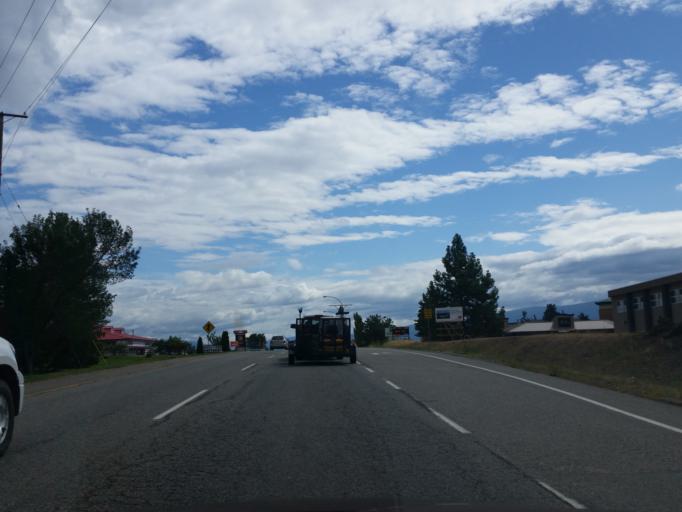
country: CA
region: British Columbia
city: West Kelowna
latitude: 49.8284
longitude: -119.6382
